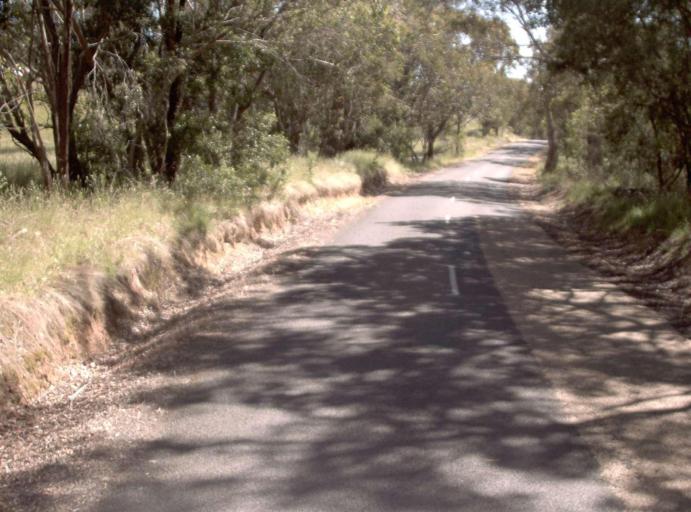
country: AU
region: New South Wales
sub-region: Bombala
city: Bombala
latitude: -37.0534
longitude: 148.8059
